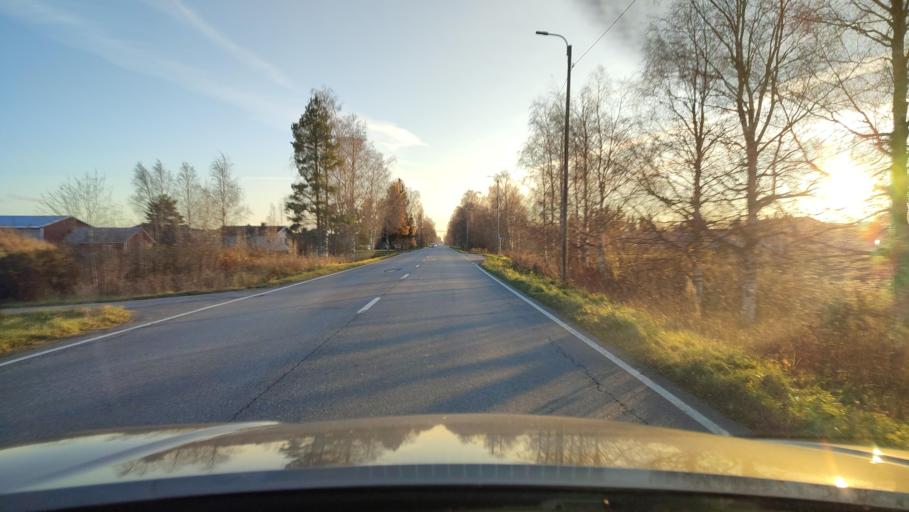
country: FI
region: Ostrobothnia
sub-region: Sydosterbotten
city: Naerpes
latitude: 62.5554
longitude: 21.4074
